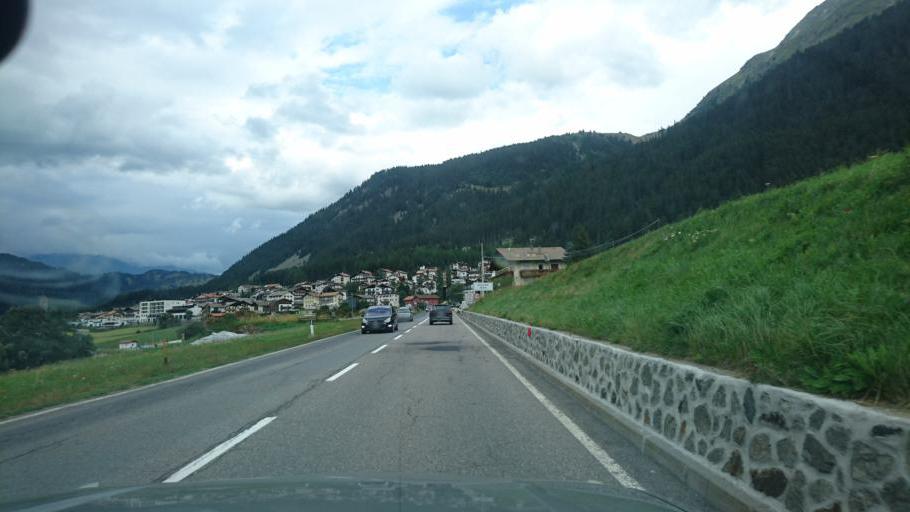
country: IT
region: Trentino-Alto Adige
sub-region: Bolzano
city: Curon Venosta
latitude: 46.8244
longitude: 10.5215
